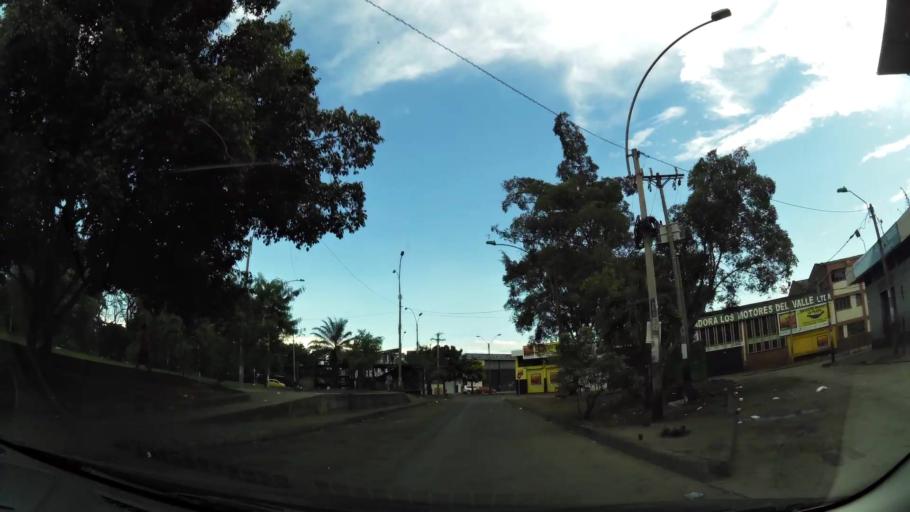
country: CO
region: Valle del Cauca
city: Cali
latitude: 3.4439
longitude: -76.5198
